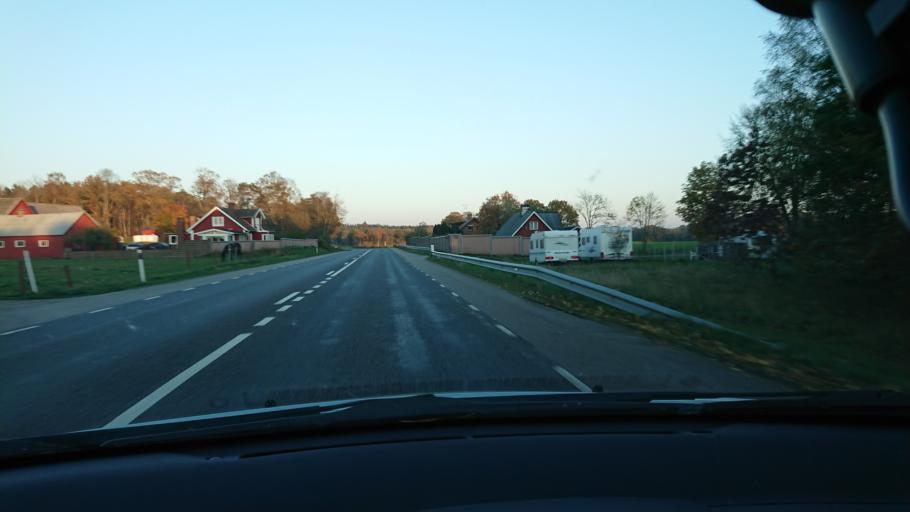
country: SE
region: Halland
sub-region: Halmstads Kommun
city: Aled
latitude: 56.6945
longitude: 12.9858
